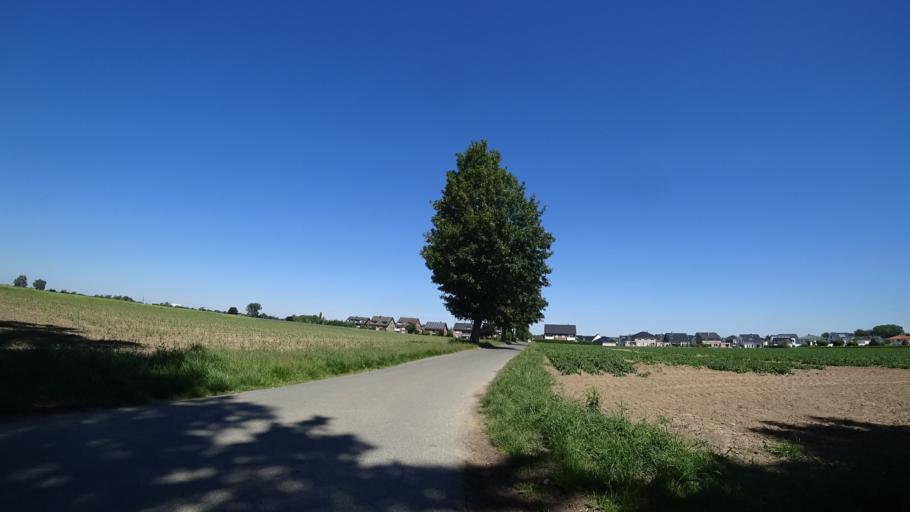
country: DE
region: North Rhine-Westphalia
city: Erwitte
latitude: 51.6211
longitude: 8.3618
